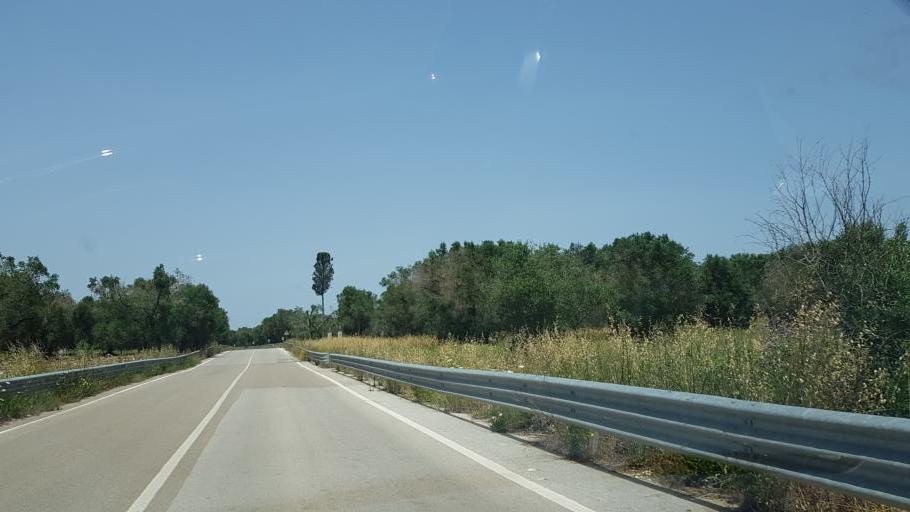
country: IT
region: Apulia
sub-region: Provincia di Brindisi
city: San Pancrazio Salentino
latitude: 40.4898
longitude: 17.8335
